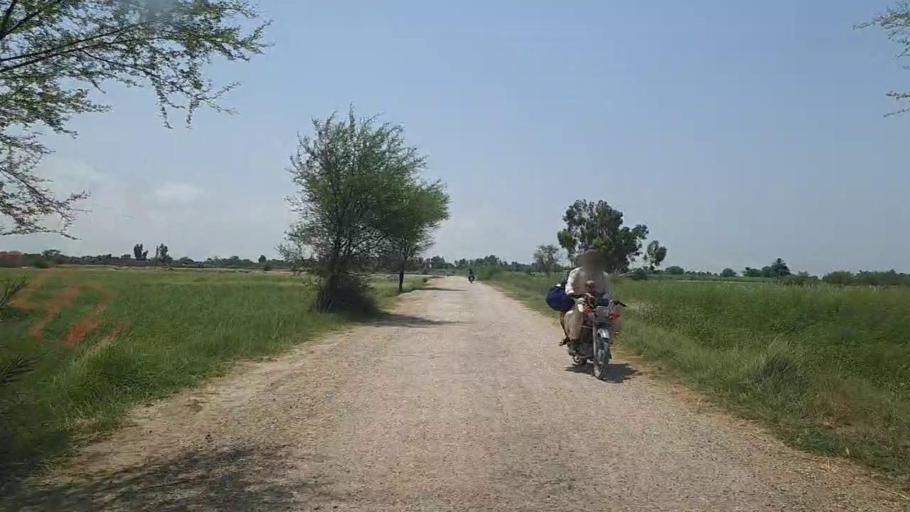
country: PK
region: Sindh
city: Ubauro
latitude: 28.1566
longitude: 69.7643
